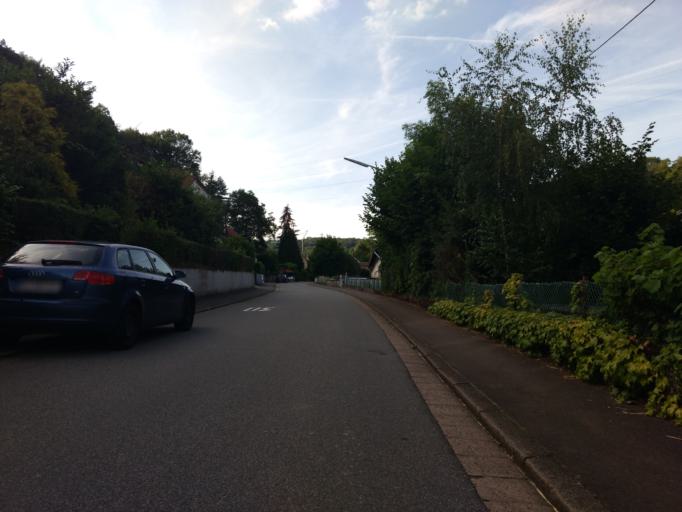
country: DE
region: Saarland
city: Beckingen
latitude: 49.3973
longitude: 6.7006
